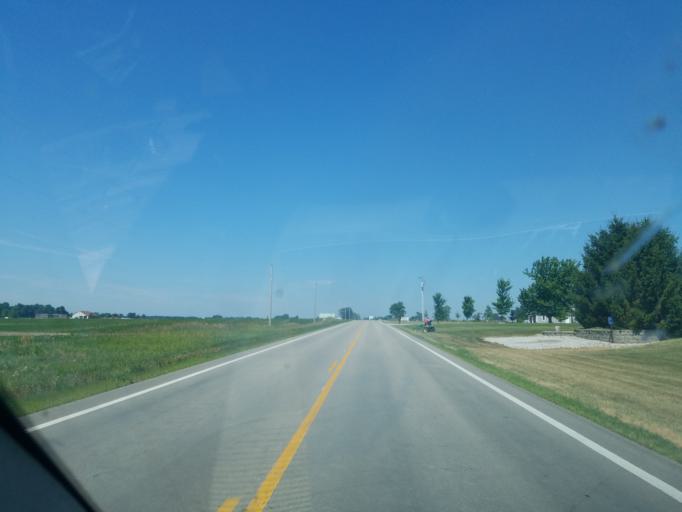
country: US
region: Ohio
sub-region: Shelby County
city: Botkins
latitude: 40.4389
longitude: -84.2430
